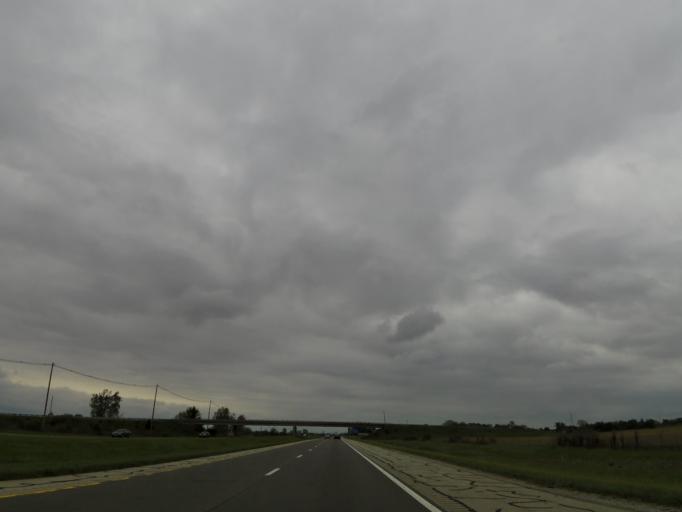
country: US
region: Ohio
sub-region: Fayette County
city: Jeffersonville
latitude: 39.6823
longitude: -83.4837
